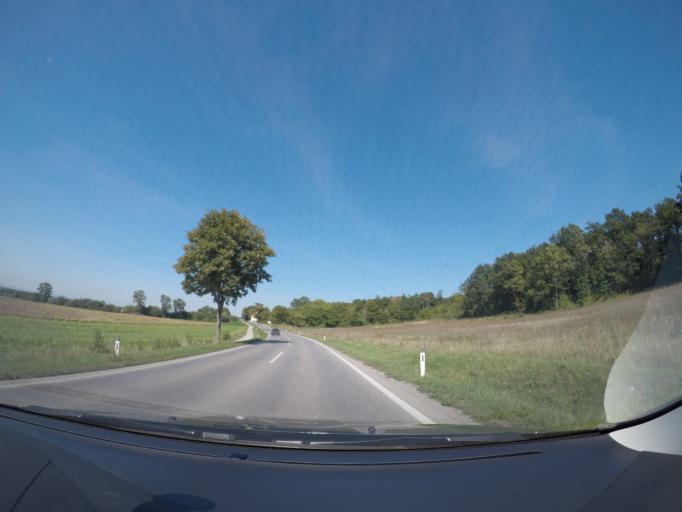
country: AT
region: Lower Austria
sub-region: Politischer Bezirk Bruck an der Leitha
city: Hof am Leithaberge
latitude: 47.9555
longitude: 16.5868
